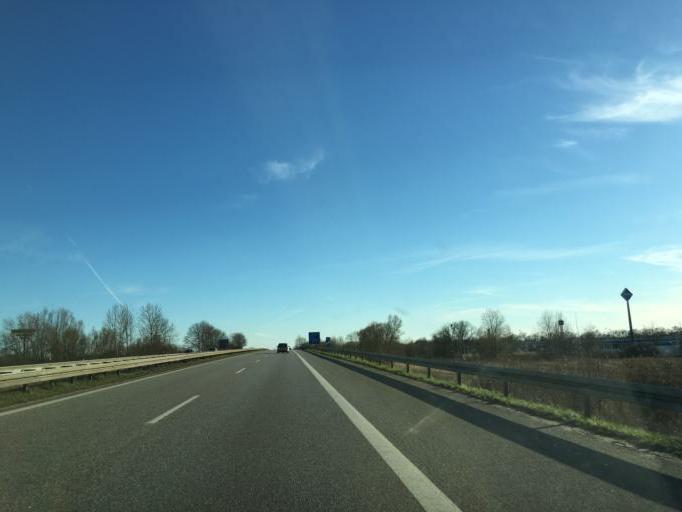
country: DE
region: Mecklenburg-Vorpommern
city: Roggentin
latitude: 54.0830
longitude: 12.1969
